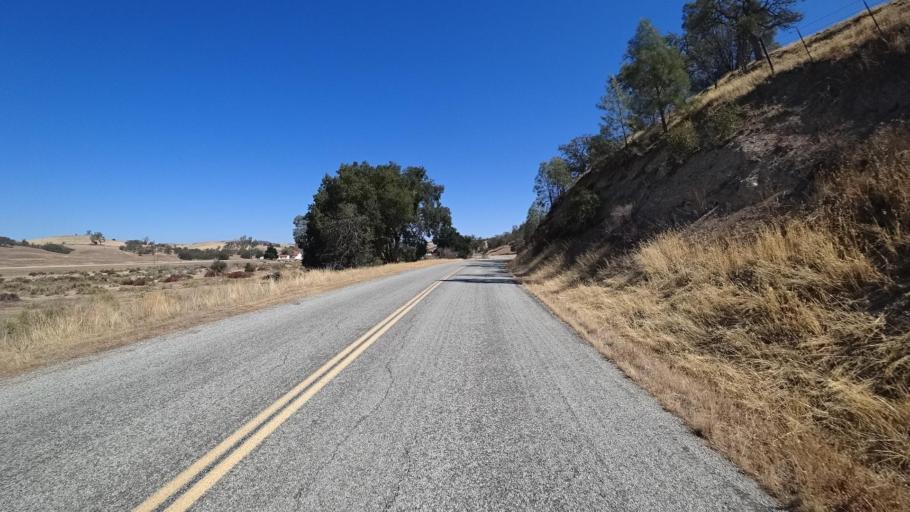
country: US
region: California
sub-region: San Luis Obispo County
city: San Miguel
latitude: 35.8403
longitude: -120.6219
